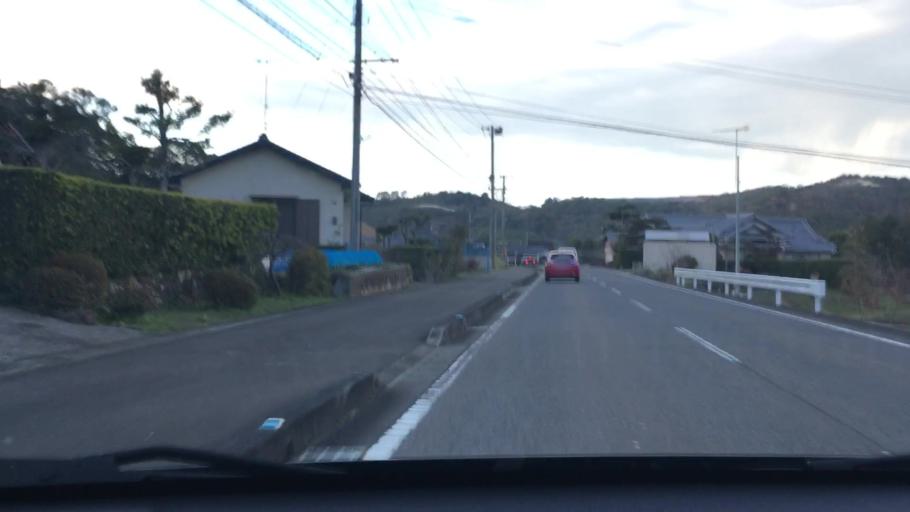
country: JP
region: Oita
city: Bungo-Takada-shi
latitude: 33.4990
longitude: 131.3759
